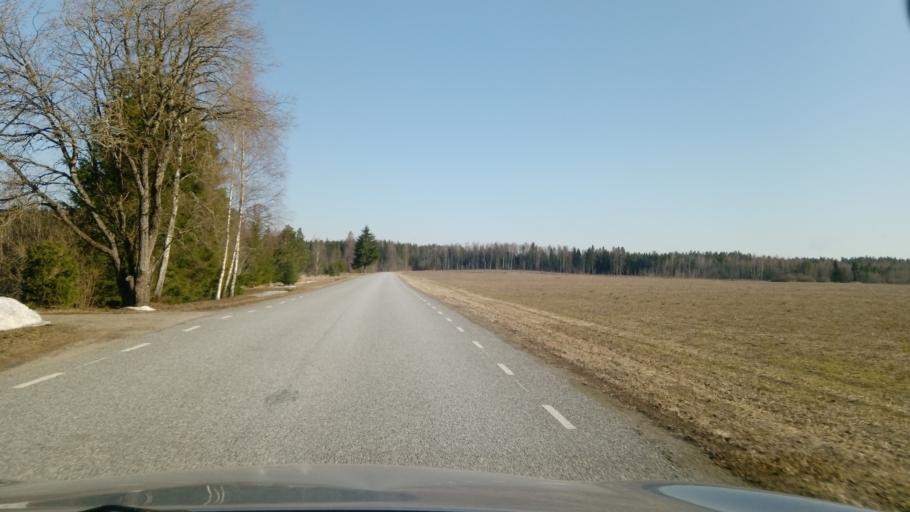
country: EE
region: Laeaene-Virumaa
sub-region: Tamsalu vald
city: Tamsalu
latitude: 59.2239
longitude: 26.1633
